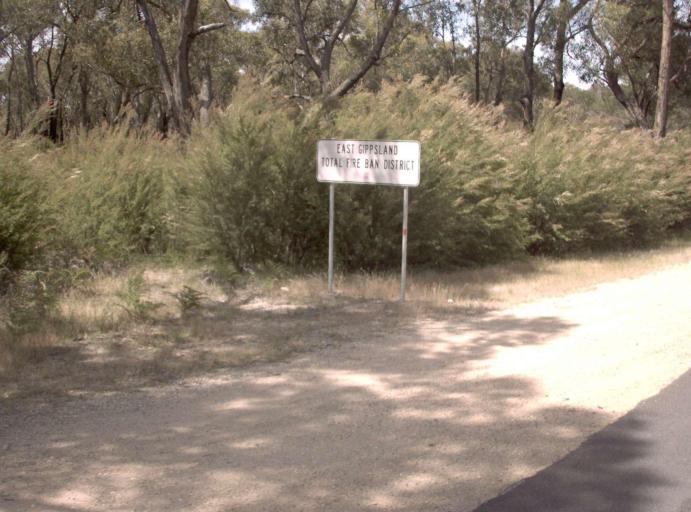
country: AU
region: Victoria
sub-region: Wellington
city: Sale
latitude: -37.9209
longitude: 147.2804
